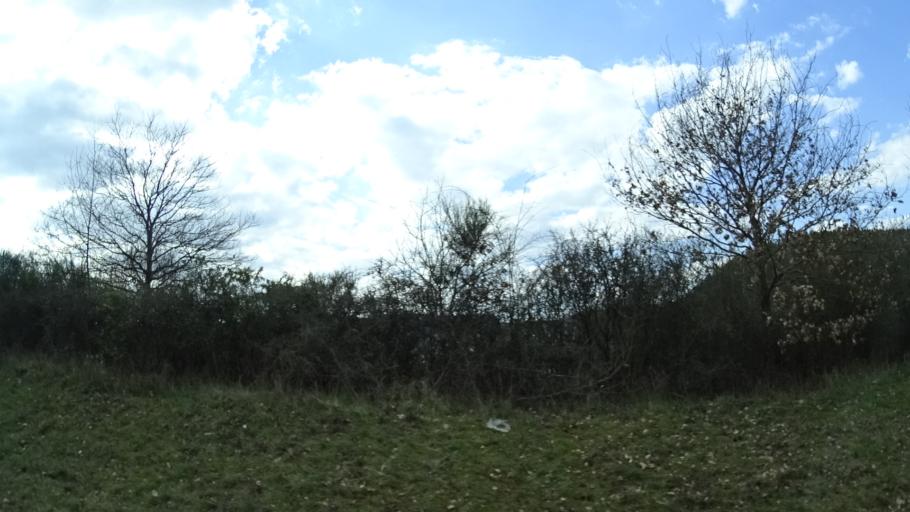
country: DE
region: Rheinland-Pfalz
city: Niederworresbach
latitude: 49.7699
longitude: 7.3415
